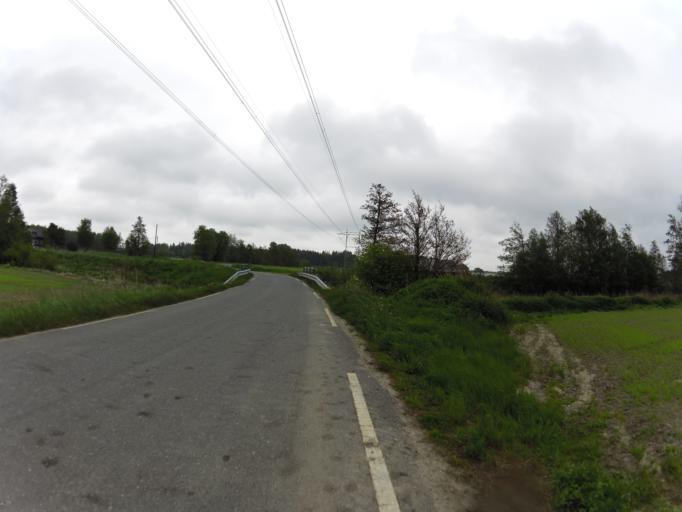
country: NO
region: Ostfold
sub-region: Rygge
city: Ryggebyen
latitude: 59.3566
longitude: 10.7401
